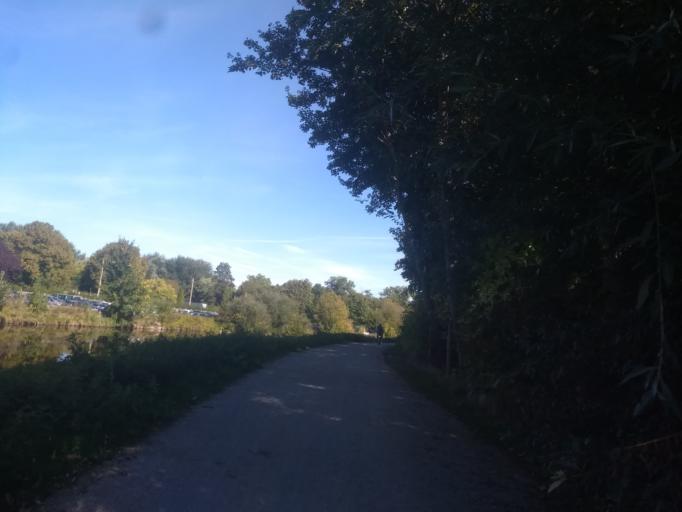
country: FR
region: Nord-Pas-de-Calais
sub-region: Departement du Pas-de-Calais
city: Fampoux
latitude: 50.2998
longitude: 2.8757
